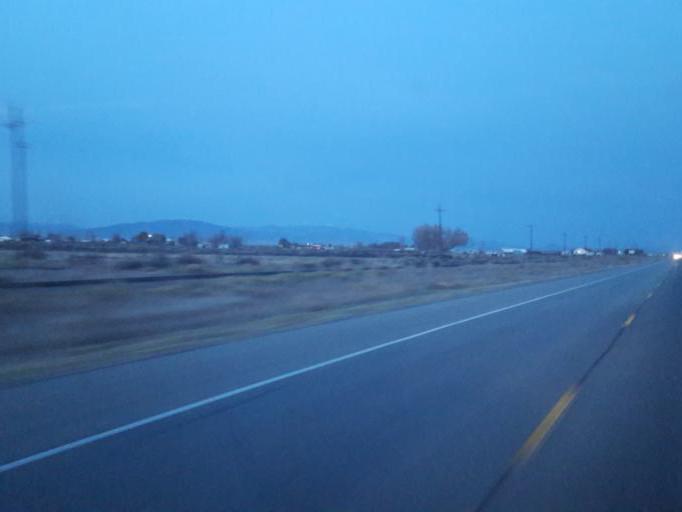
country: US
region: Colorado
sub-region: Alamosa County
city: Alamosa
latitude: 37.4958
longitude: -105.9431
